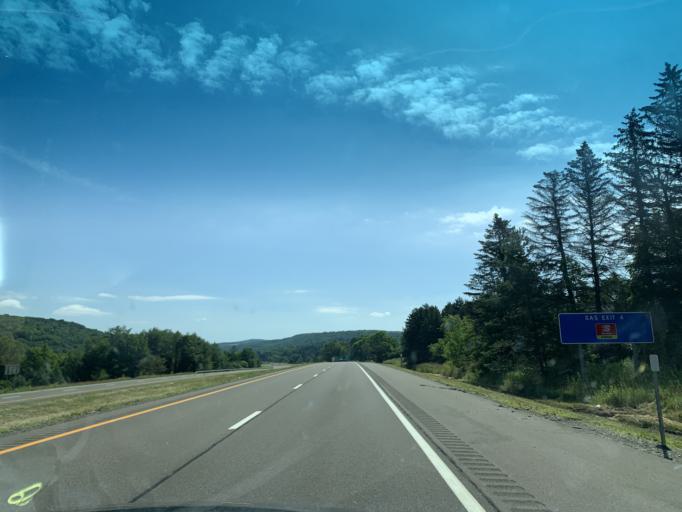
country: US
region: New York
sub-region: Broome County
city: Chenango Bridge
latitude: 42.1605
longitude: -75.7820
